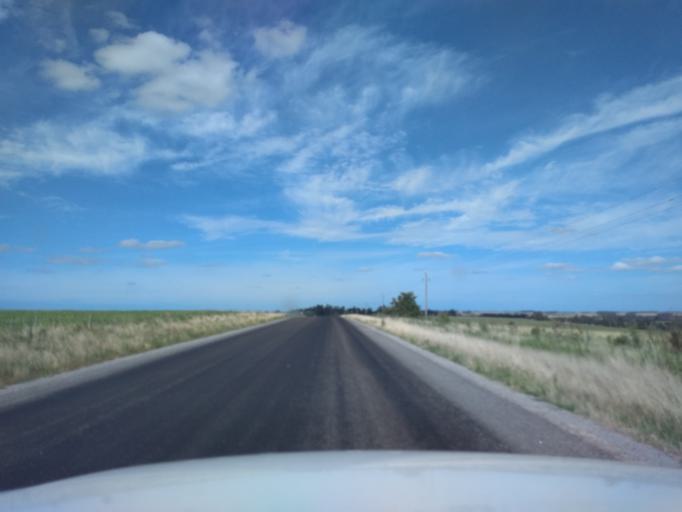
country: UY
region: Florida
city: Casupa
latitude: -34.0290
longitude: -55.8713
